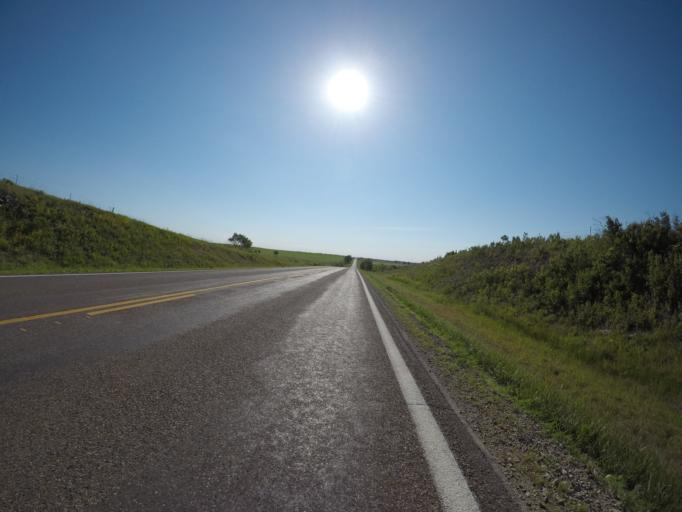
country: US
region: Kansas
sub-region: Morris County
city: Council Grove
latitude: 38.6590
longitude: -96.2486
